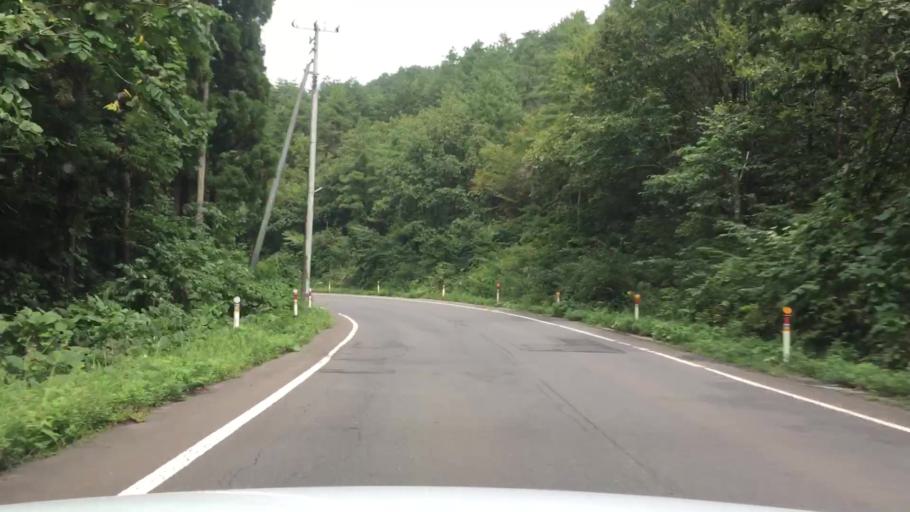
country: JP
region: Aomori
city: Shimokizukuri
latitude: 40.7216
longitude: 140.2584
